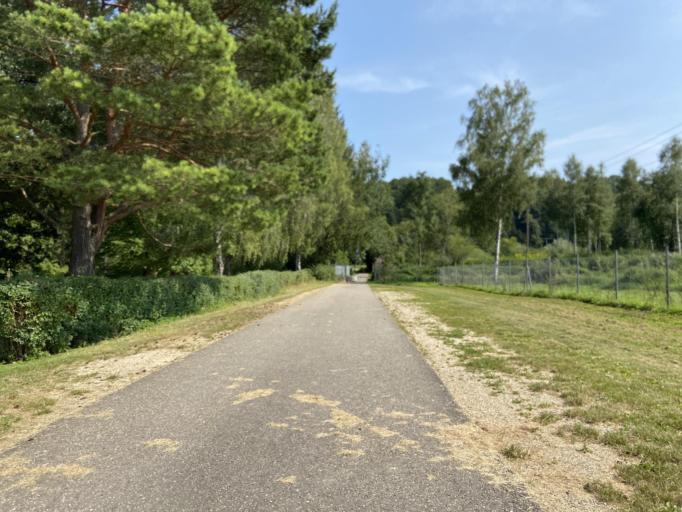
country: DE
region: Baden-Wuerttemberg
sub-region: Tuebingen Region
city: Bingen
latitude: 48.0903
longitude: 9.2783
